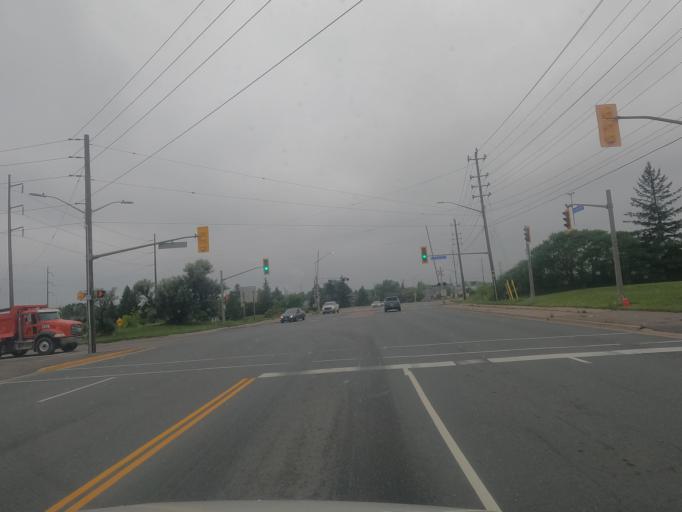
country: CA
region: Ontario
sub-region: Algoma
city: Sault Ste. Marie
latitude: 46.5384
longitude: -84.3455
